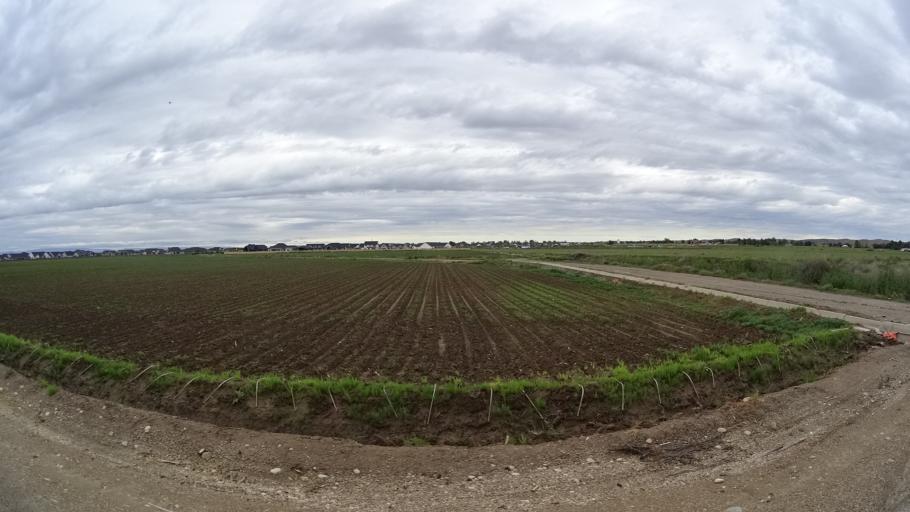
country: US
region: Idaho
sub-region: Ada County
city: Eagle
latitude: 43.7134
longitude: -116.4135
